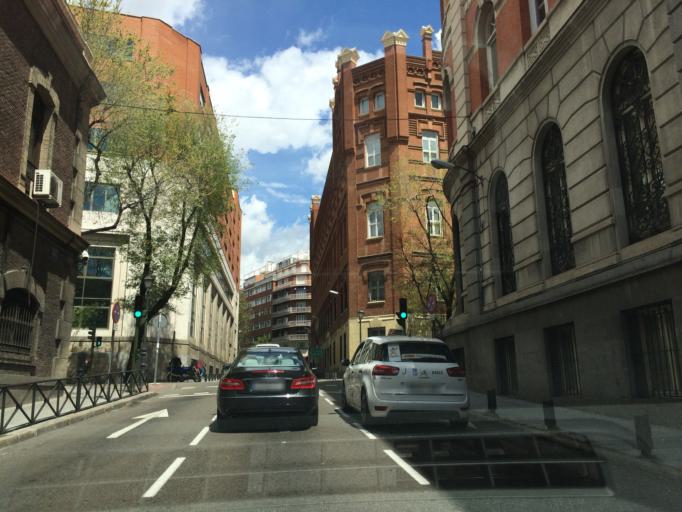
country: ES
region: Madrid
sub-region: Provincia de Madrid
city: Chamberi
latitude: 40.4292
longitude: -3.7126
